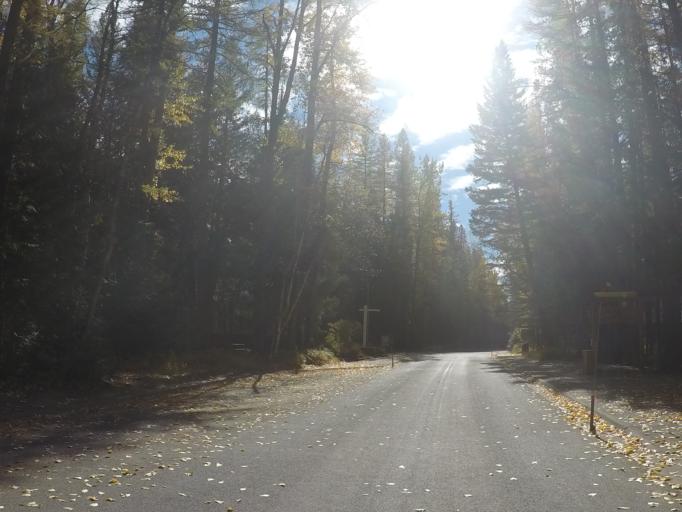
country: US
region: Montana
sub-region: Flathead County
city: Columbia Falls
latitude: 48.5271
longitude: -113.9938
